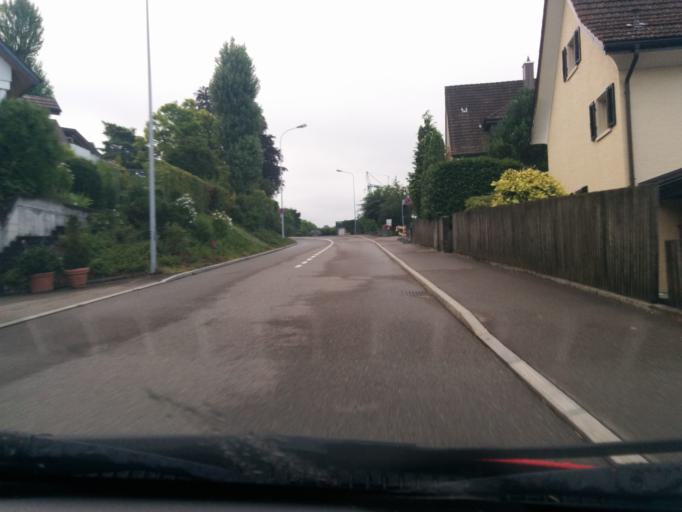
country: CH
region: Zurich
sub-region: Bezirk Meilen
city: Kuesnacht / Heslibach
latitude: 47.3130
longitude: 8.5911
